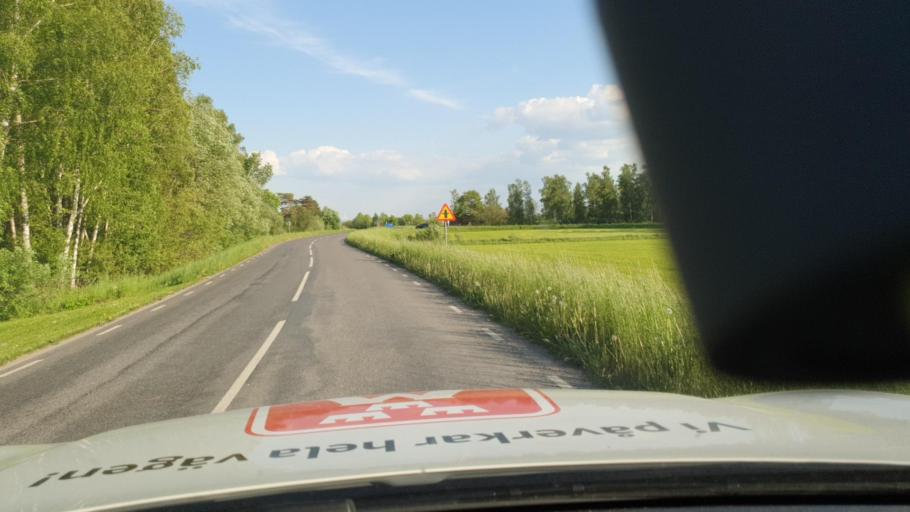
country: SE
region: Vaestra Goetaland
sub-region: Falkopings Kommun
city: Akarp
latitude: 58.1799
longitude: 13.6335
